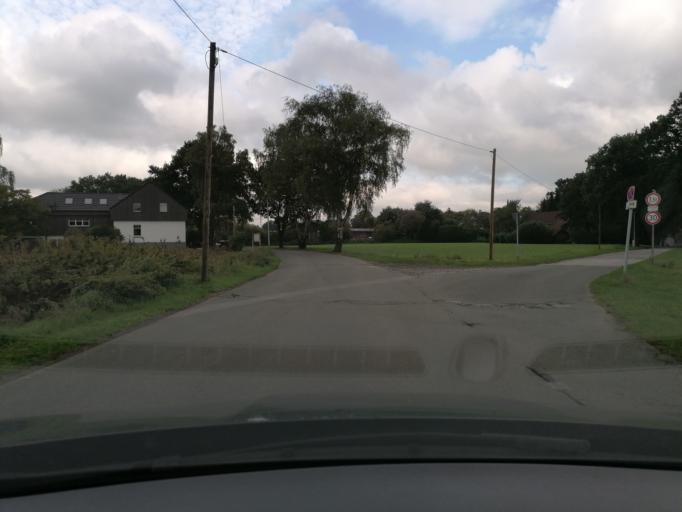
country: DE
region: North Rhine-Westphalia
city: Herten
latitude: 51.5739
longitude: 7.0998
